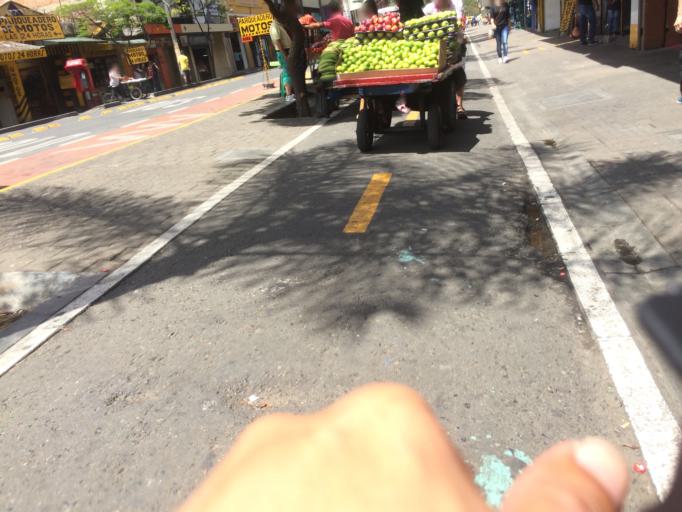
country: CO
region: Antioquia
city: Medellin
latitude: 6.2542
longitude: -75.5683
